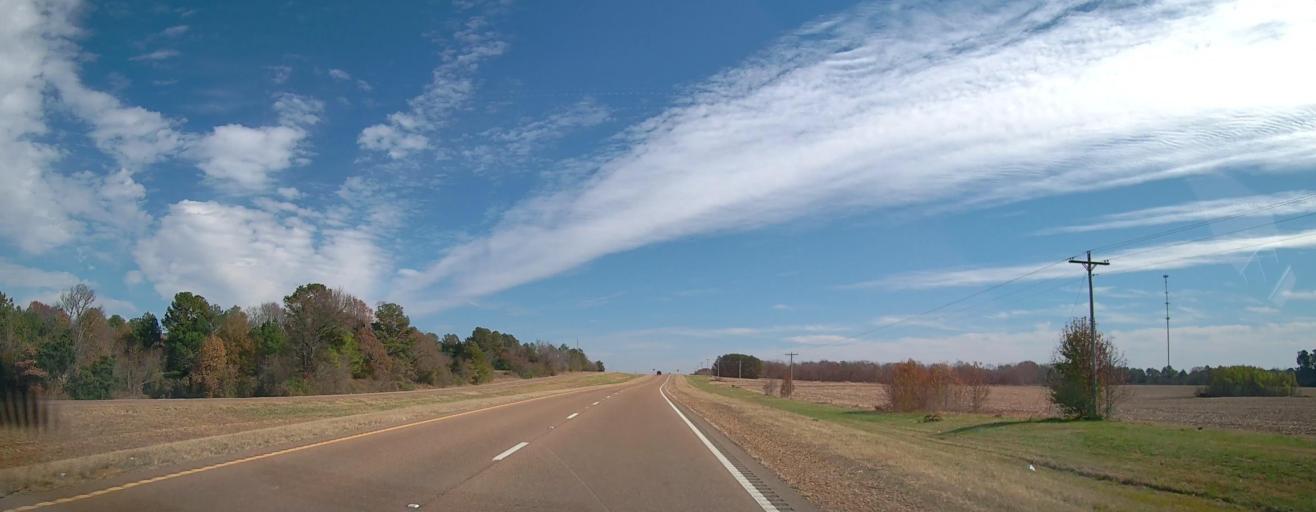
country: US
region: Mississippi
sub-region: Benton County
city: Ashland
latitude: 34.9461
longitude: -89.3239
